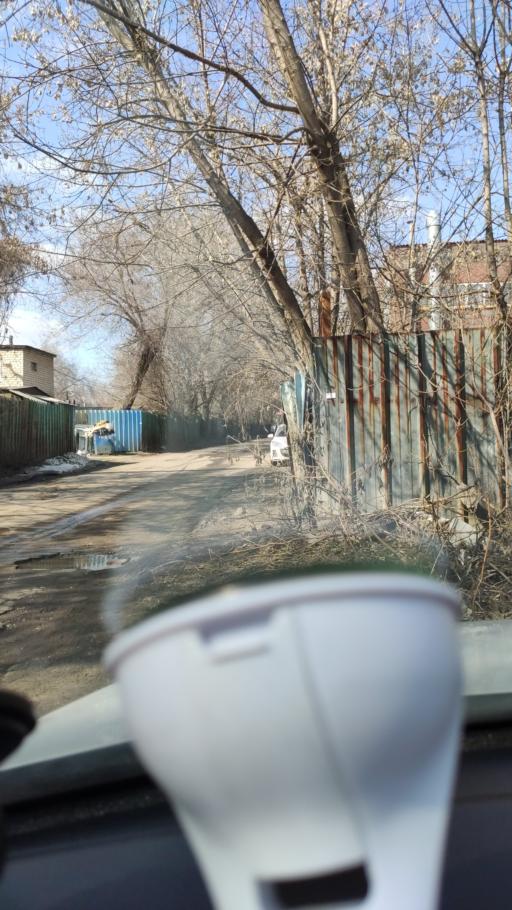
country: RU
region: Samara
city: Samara
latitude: 53.1792
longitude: 50.1937
